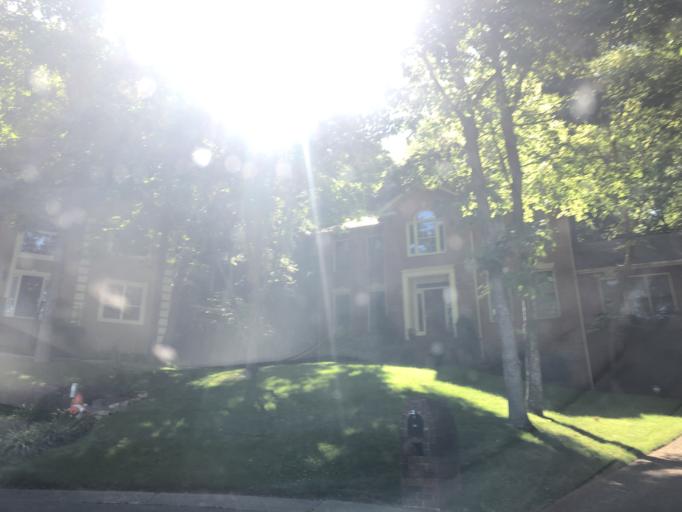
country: US
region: Tennessee
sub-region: Davidson County
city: Belle Meade
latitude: 36.0668
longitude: -86.9187
